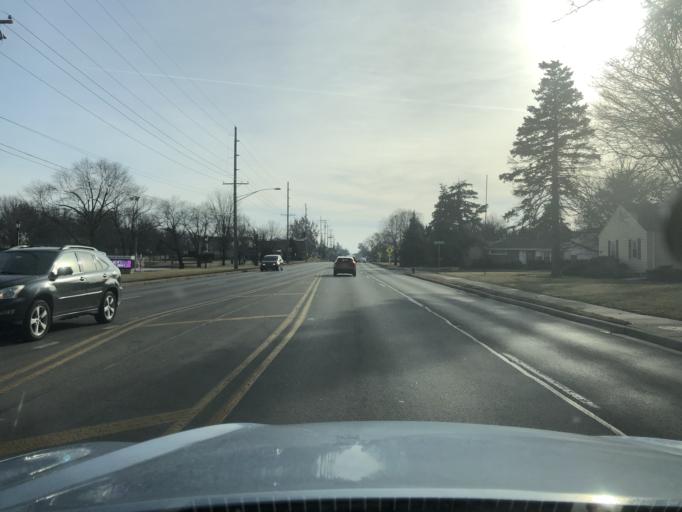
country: US
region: Illinois
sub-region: DuPage County
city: Roselle
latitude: 41.9903
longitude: -88.0804
